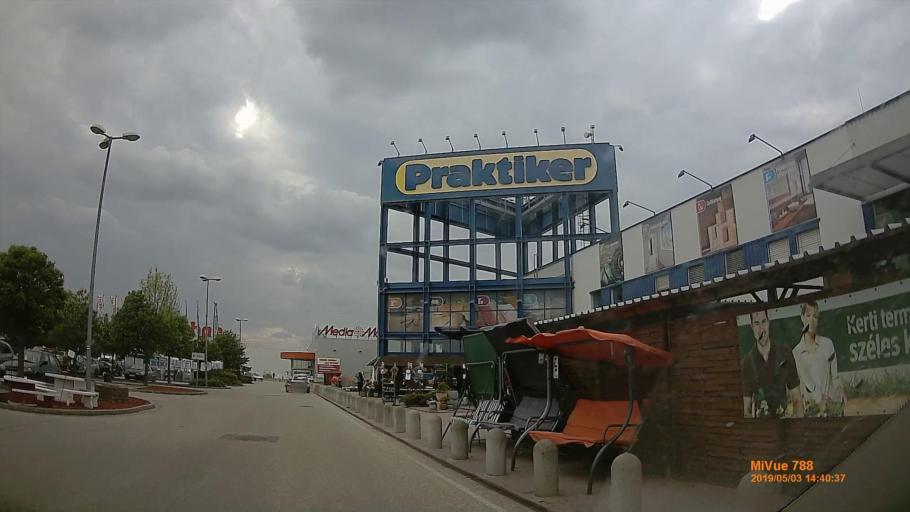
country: HU
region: Jasz-Nagykun-Szolnok
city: Szolnok
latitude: 47.1609
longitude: 20.2001
